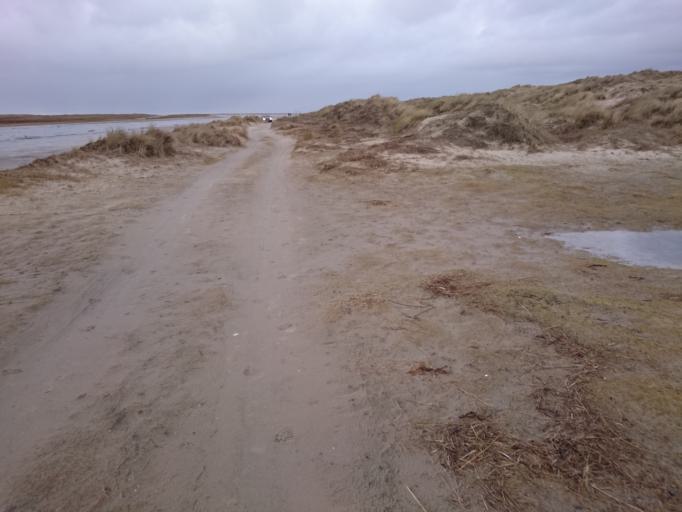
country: DK
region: South Denmark
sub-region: Fano Kommune
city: Nordby
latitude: 55.4258
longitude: 8.3700
